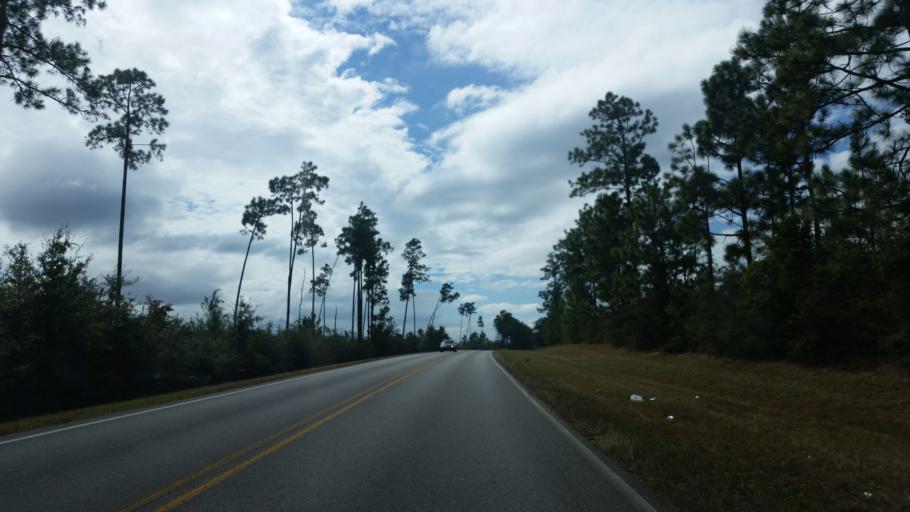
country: US
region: Florida
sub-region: Santa Rosa County
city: Point Baker
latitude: 30.7278
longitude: -86.9535
